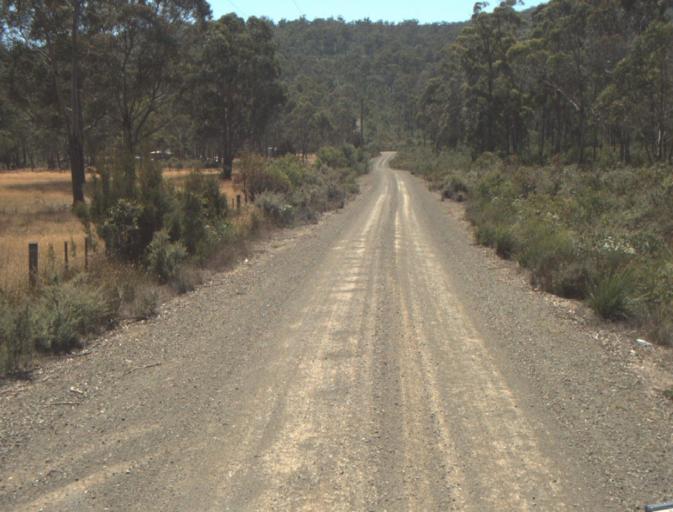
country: AU
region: Tasmania
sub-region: Launceston
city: Mayfield
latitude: -41.2751
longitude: 147.0989
